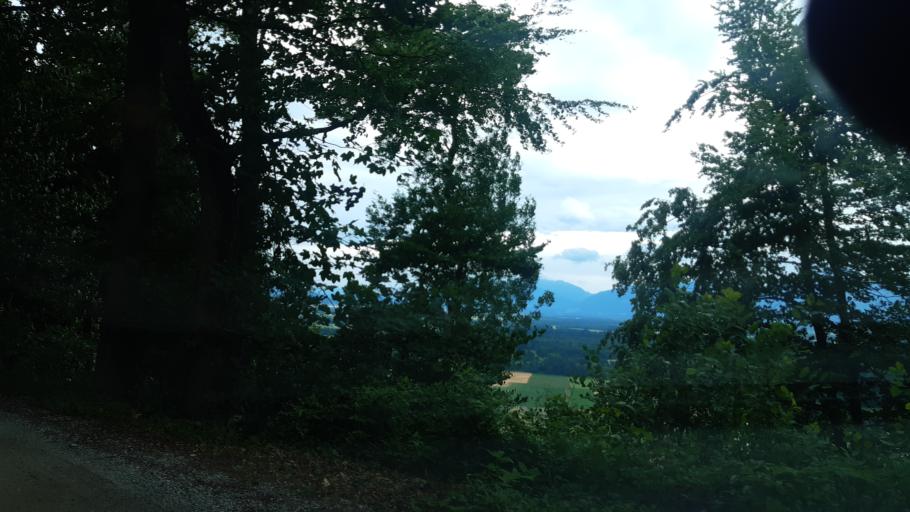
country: SI
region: Medvode
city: Zgornje Pirnice
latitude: 46.1656
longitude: 14.4441
